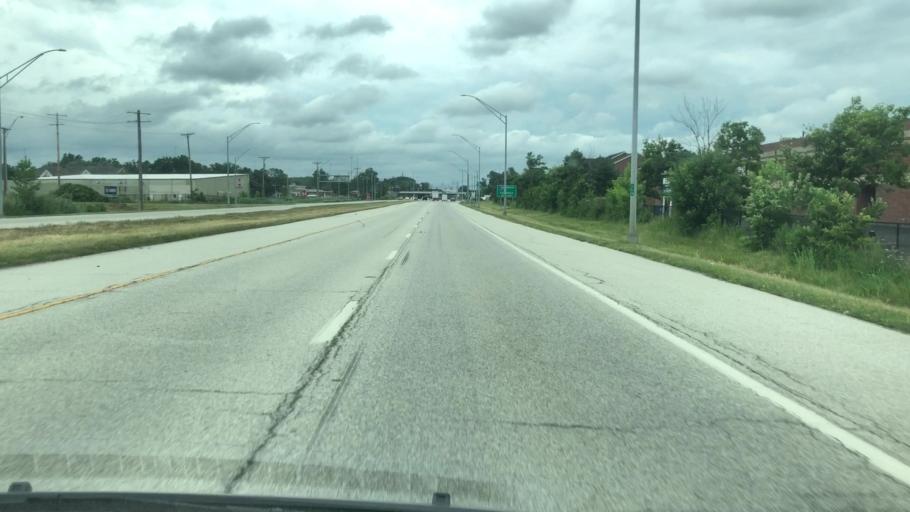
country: US
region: Ohio
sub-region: Summit County
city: Macedonia
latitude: 41.2959
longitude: -81.5130
